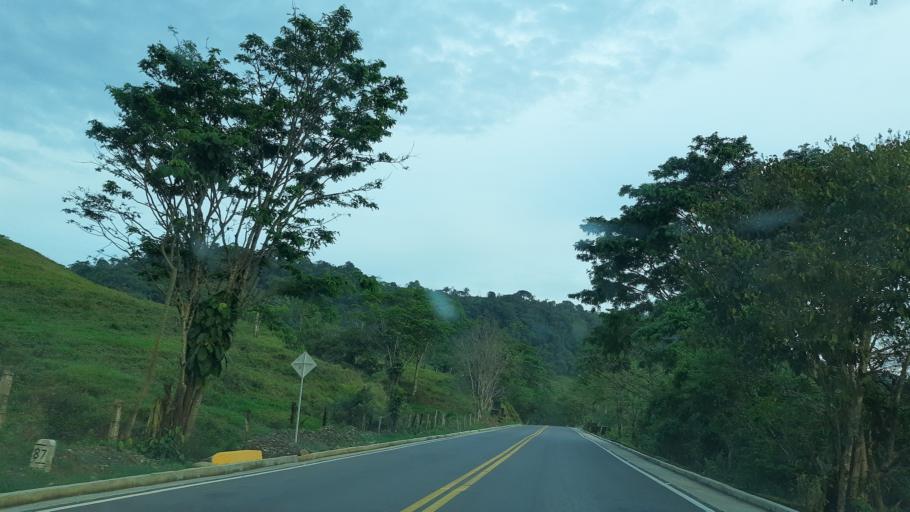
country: CO
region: Casanare
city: Sabanalarga
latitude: 4.7713
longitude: -73.0326
